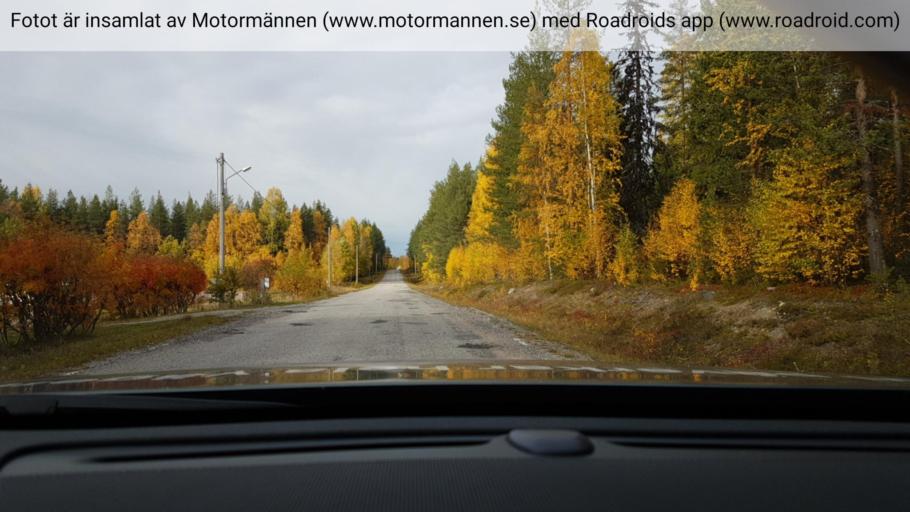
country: SE
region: Norrbotten
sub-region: Overkalix Kommun
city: OEverkalix
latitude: 66.2493
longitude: 23.1343
